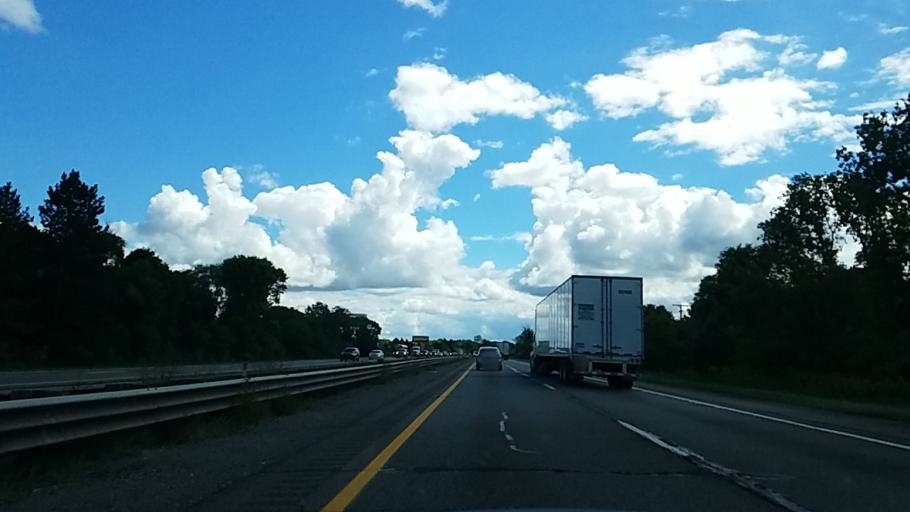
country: US
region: Michigan
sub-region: Livingston County
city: Whitmore Lake
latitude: 42.4161
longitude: -83.7658
